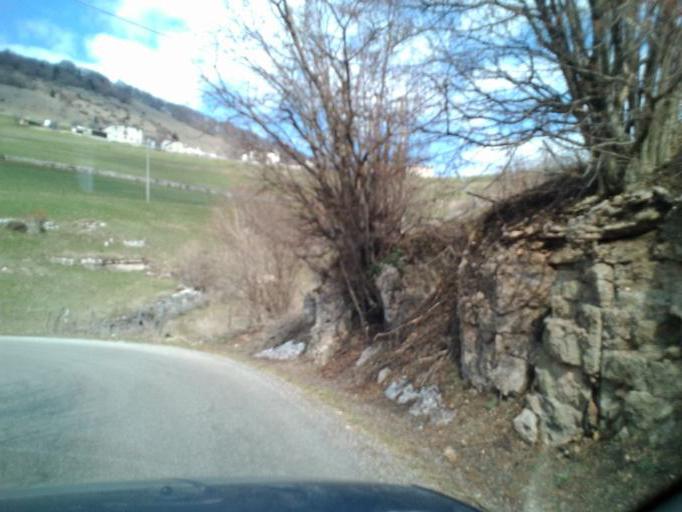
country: IT
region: Veneto
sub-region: Provincia di Verona
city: Erbezzo
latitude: 45.6490
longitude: 10.9957
